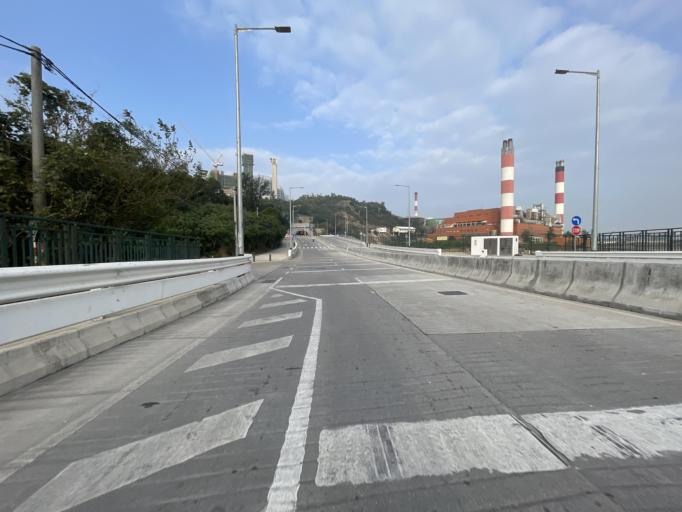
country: MO
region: Macau
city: Macau
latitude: 22.1348
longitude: 113.5813
